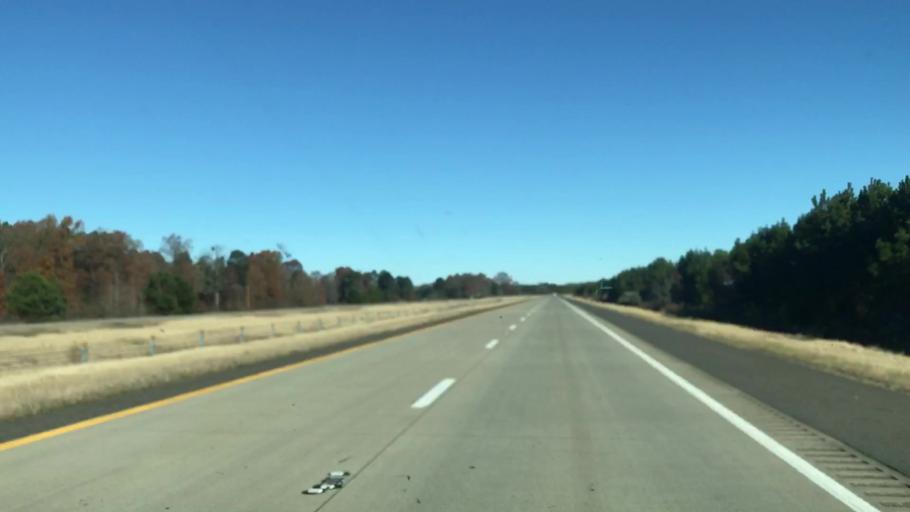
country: US
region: Texas
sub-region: Cass County
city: Queen City
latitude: 33.1924
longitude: -93.8774
